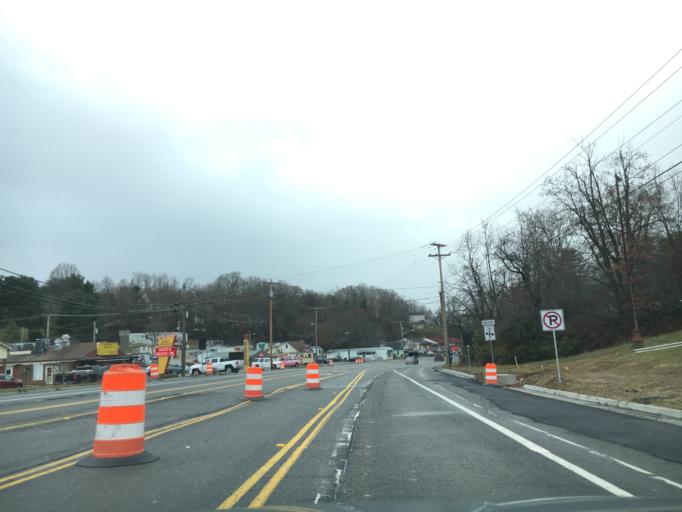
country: US
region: Virginia
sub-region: Montgomery County
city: Christiansburg
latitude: 37.1326
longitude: -80.3791
